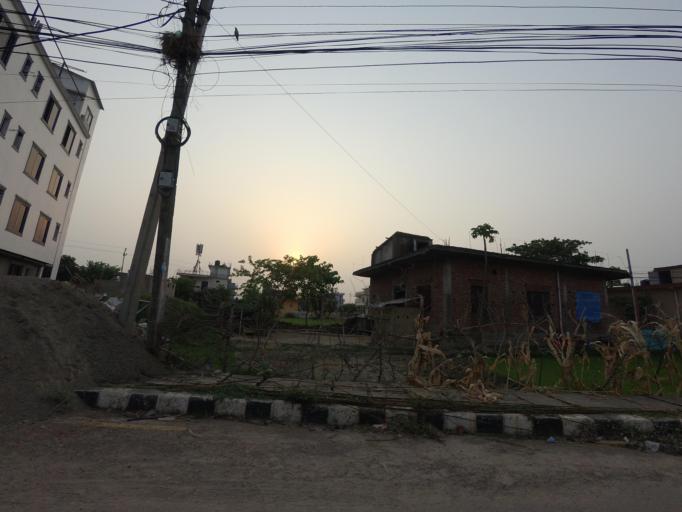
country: NP
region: Western Region
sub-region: Lumbini Zone
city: Bhairahawa
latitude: 27.5128
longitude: 83.4630
